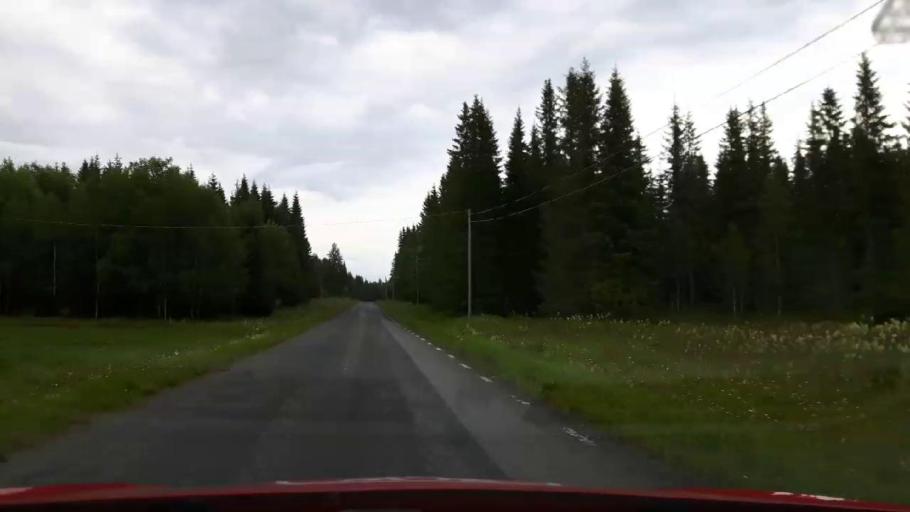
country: SE
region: Jaemtland
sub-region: OEstersunds Kommun
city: Lit
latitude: 63.3694
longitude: 15.1682
